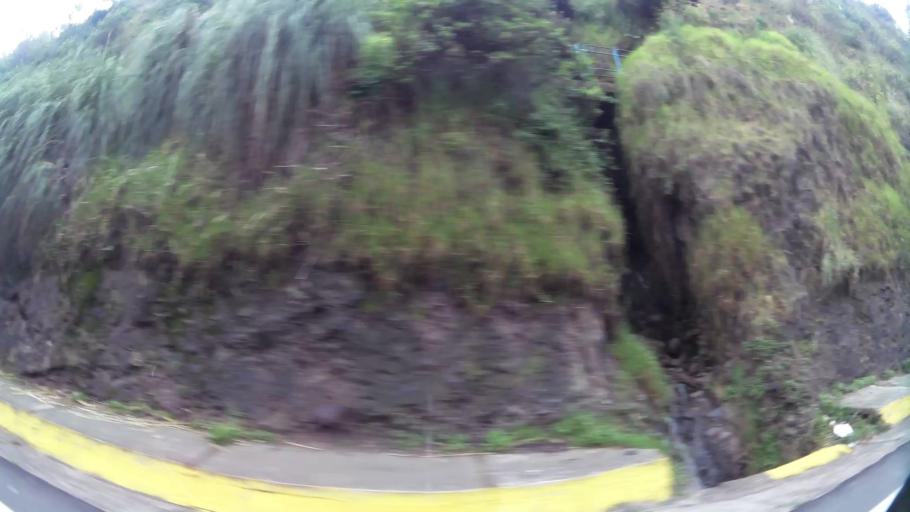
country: EC
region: Pichincha
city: Quito
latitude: -0.2316
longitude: -78.4993
